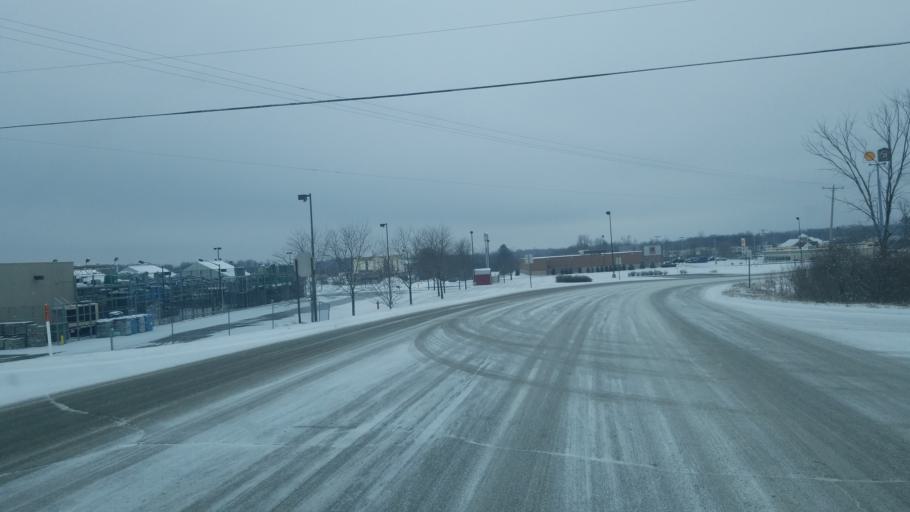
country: US
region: Michigan
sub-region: Mecosta County
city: Big Rapids
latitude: 43.6852
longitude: -85.5140
